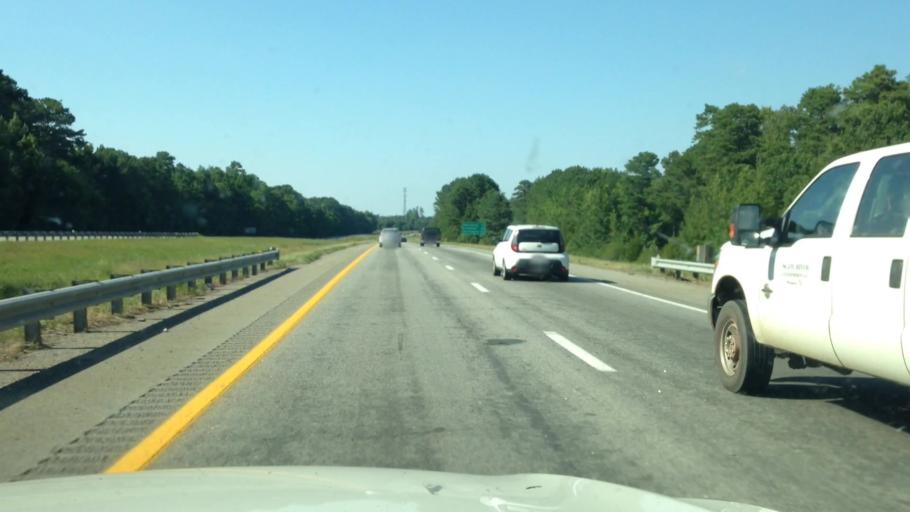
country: US
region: Virginia
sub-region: City of Emporia
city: Emporia
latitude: 36.8169
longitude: -77.4559
